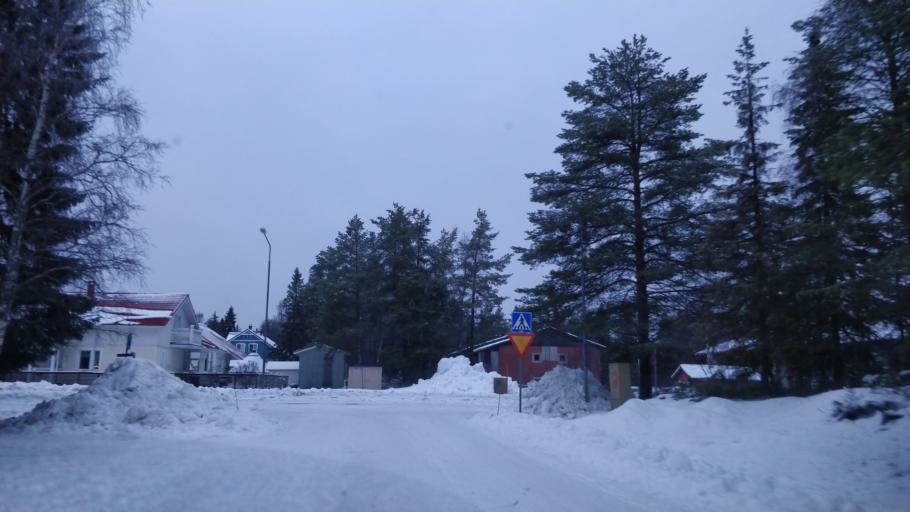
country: FI
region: Lapland
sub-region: Kemi-Tornio
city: Kemi
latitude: 65.7428
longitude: 24.6011
